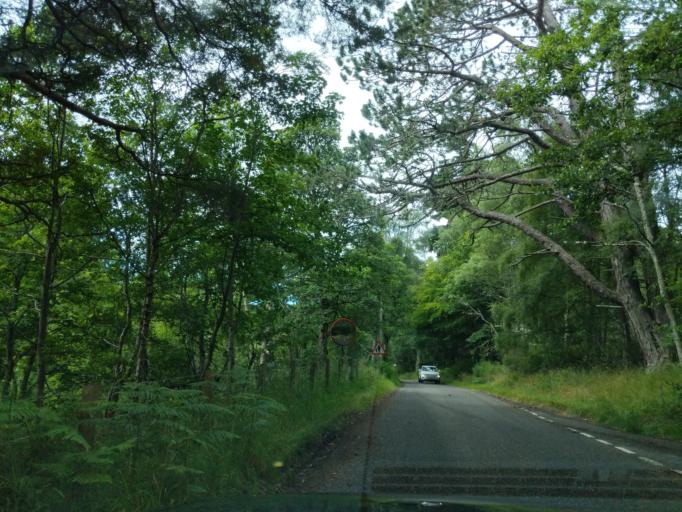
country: GB
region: Scotland
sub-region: Aberdeenshire
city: Aboyne
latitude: 57.0573
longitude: -2.8565
